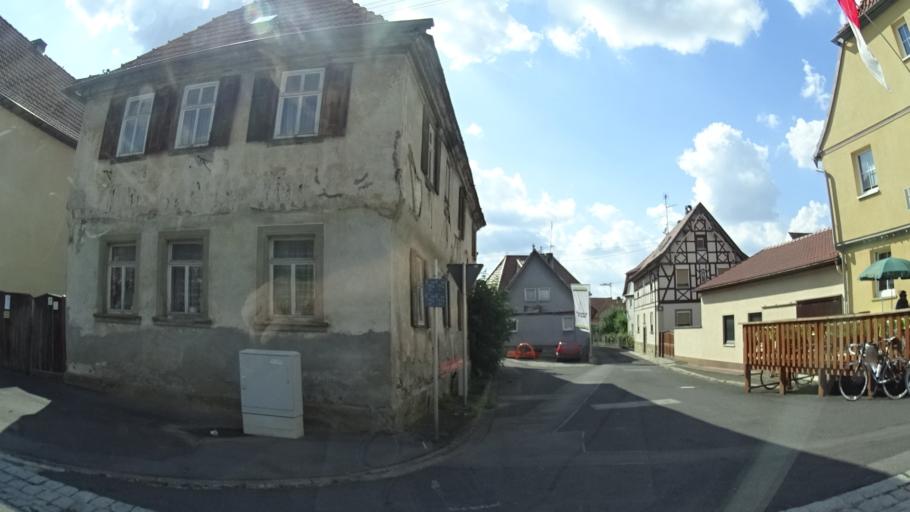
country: DE
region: Bavaria
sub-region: Regierungsbezirk Unterfranken
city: Trappstadt
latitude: 50.3191
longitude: 10.5707
